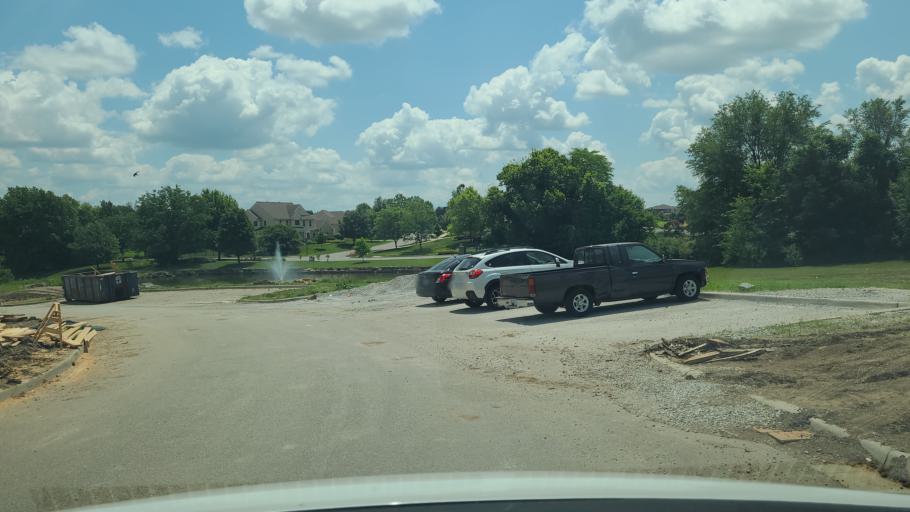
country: US
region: Kansas
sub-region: Douglas County
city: Lawrence
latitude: 38.9820
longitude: -95.3125
